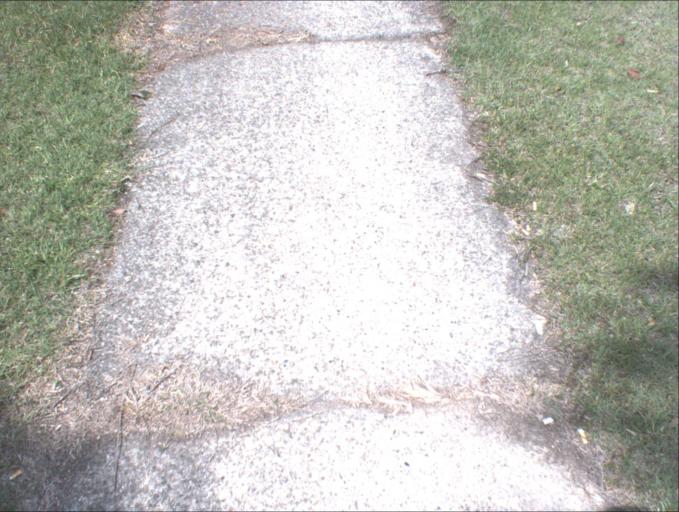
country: AU
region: Queensland
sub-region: Logan
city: Park Ridge South
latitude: -27.6842
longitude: 153.0364
